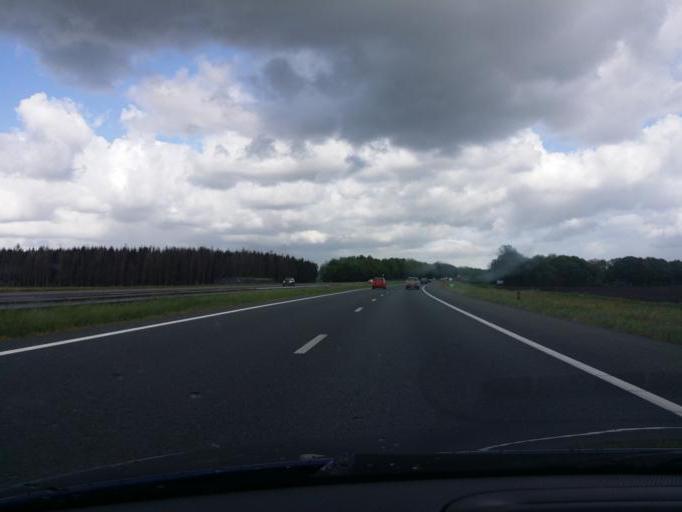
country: NL
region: Groningen
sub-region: Gemeente Haren
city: Haren
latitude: 53.2003
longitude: 6.6782
